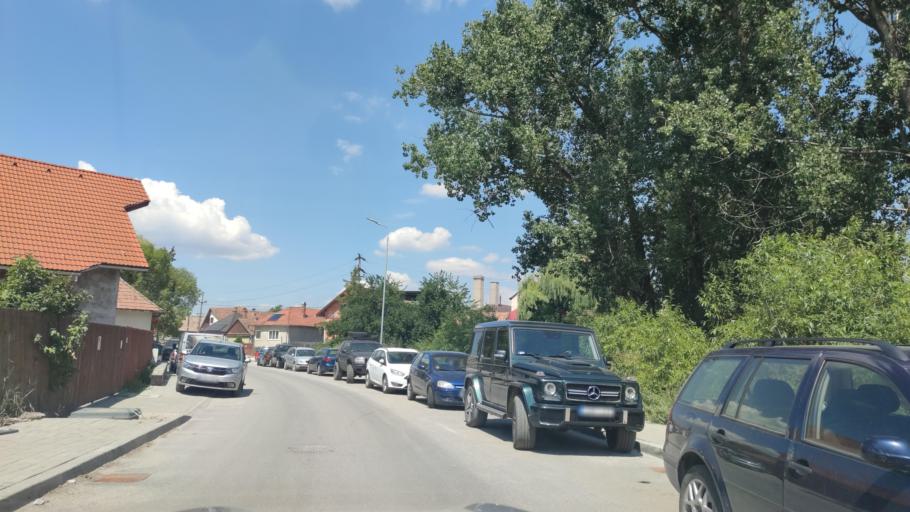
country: RO
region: Harghita
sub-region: Municipiul Gheorgheni
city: Gheorgheni
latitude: 46.7187
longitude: 25.5988
